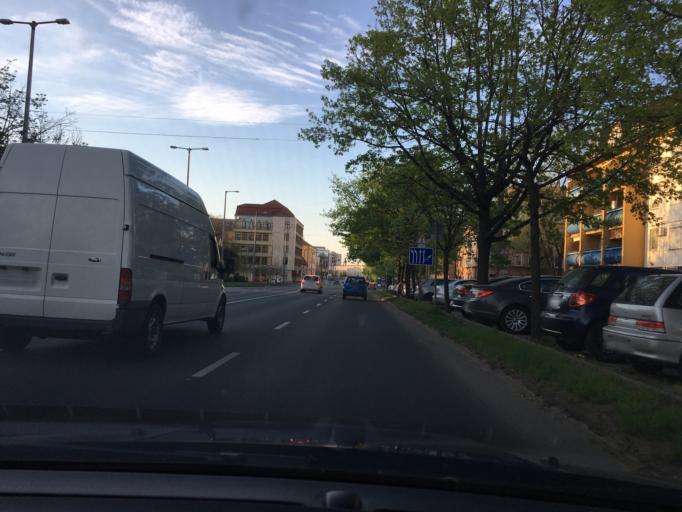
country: HU
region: Hajdu-Bihar
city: Debrecen
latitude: 47.5259
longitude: 21.6324
